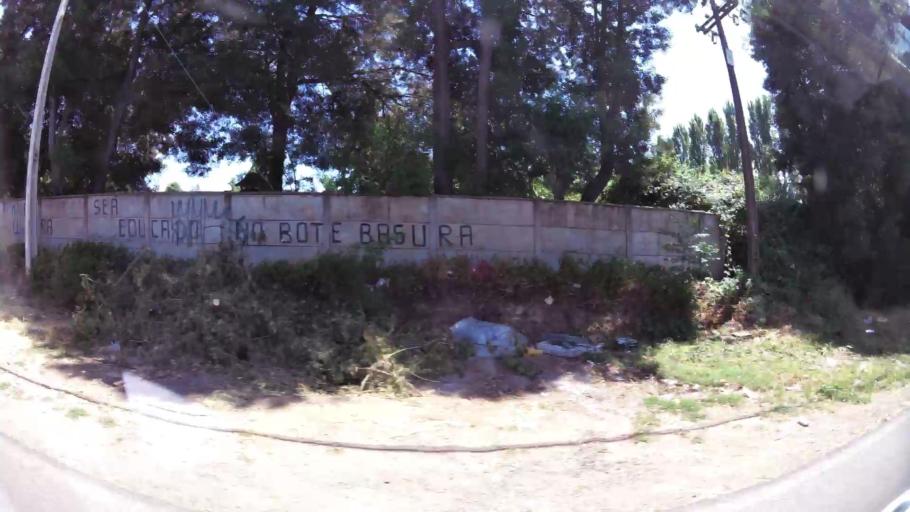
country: CL
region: Maule
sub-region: Provincia de Talca
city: Talca
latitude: -35.4427
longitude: -71.6151
